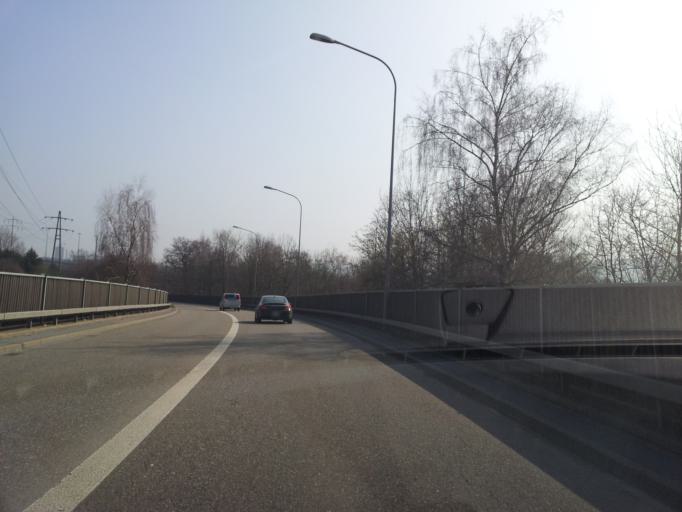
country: CH
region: Zurich
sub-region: Bezirk Zuerich
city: Zuerich (Kreis 12) / Saatlen
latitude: 47.4129
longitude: 8.5672
